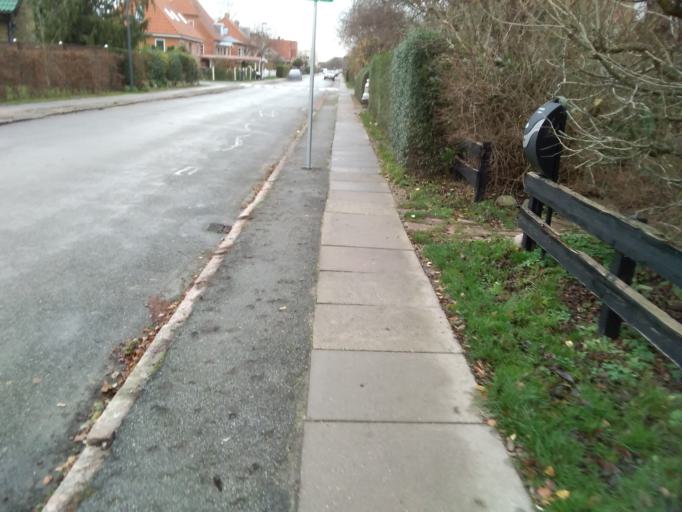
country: DK
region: Capital Region
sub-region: Tarnby Kommune
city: Tarnby
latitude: 55.6416
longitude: 12.6218
